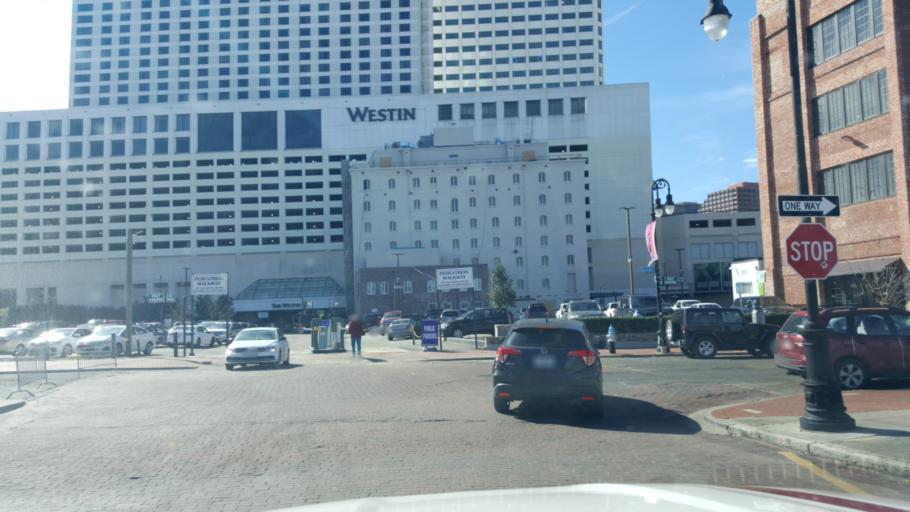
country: US
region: Louisiana
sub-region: Orleans Parish
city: New Orleans
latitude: 29.9528
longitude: -90.0641
